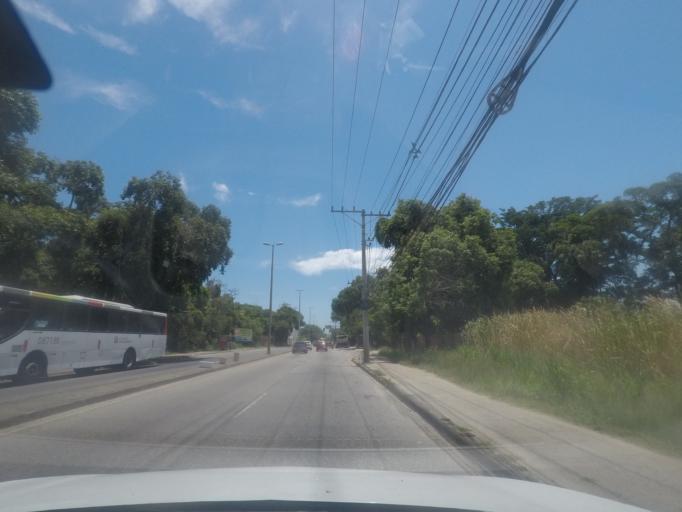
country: BR
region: Rio de Janeiro
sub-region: Itaguai
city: Itaguai
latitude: -22.8961
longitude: -43.6771
